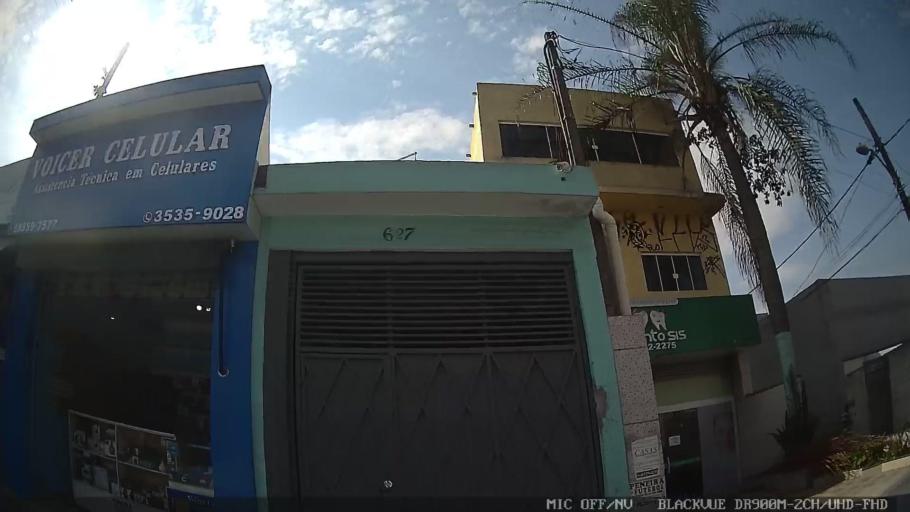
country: BR
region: Sao Paulo
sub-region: Ferraz De Vasconcelos
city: Ferraz de Vasconcelos
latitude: -23.5360
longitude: -46.4030
